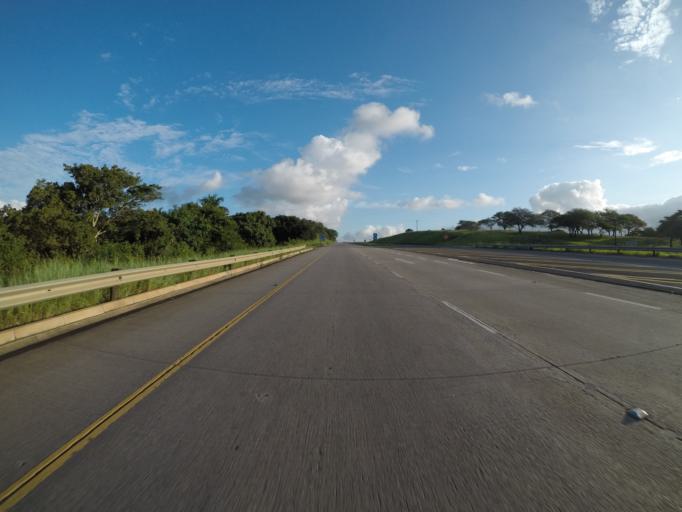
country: ZA
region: KwaZulu-Natal
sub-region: uMkhanyakude District Municipality
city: Mtubatuba
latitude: -28.5046
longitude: 32.1375
